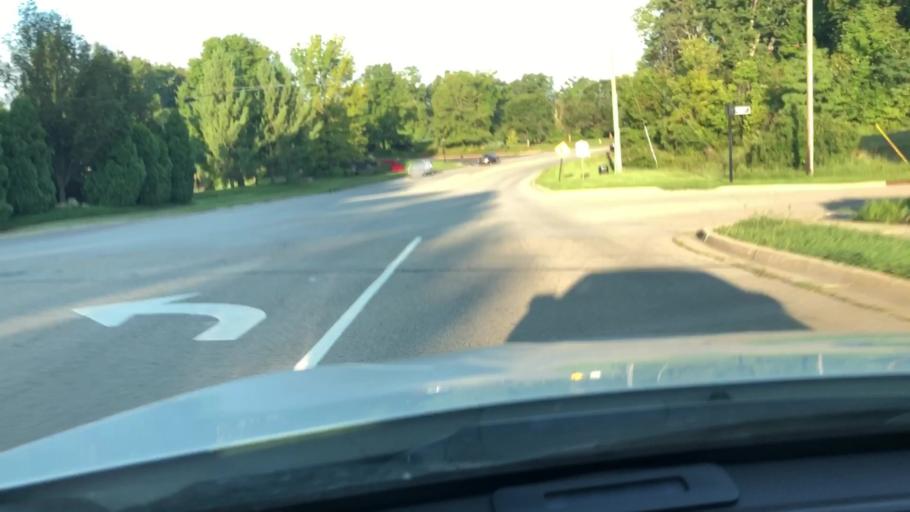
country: US
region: Kentucky
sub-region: Jefferson County
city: Middletown
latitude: 38.2167
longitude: -85.5309
